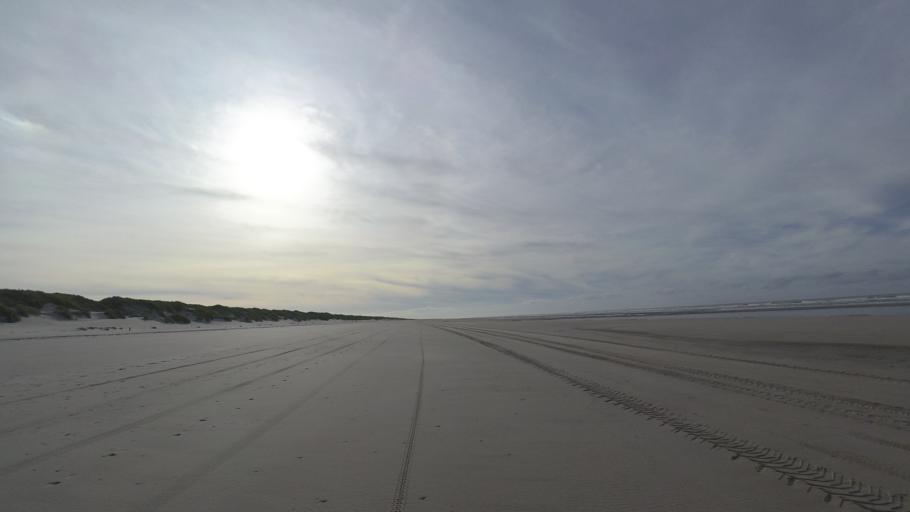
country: NL
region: Friesland
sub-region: Gemeente Ameland
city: Nes
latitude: 53.4654
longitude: 5.8599
